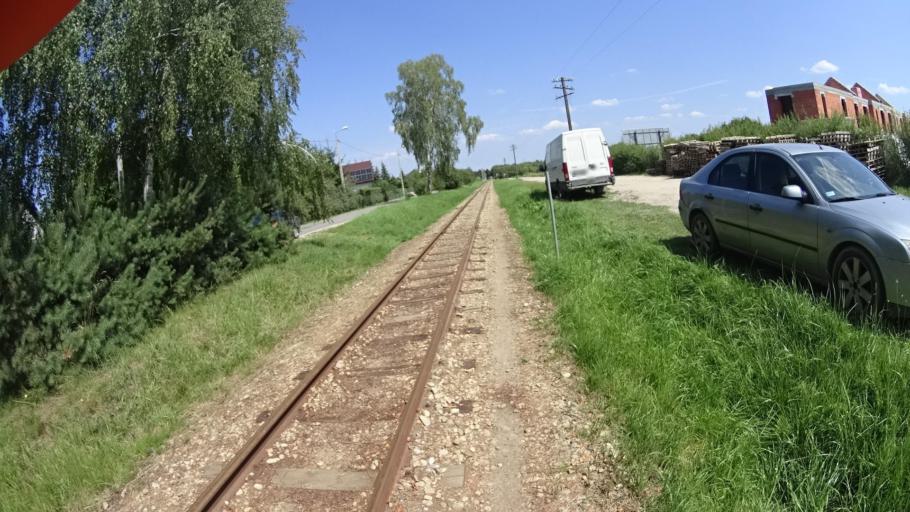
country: PL
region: Masovian Voivodeship
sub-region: Powiat piaseczynski
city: Lesznowola
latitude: 52.0235
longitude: 20.9415
